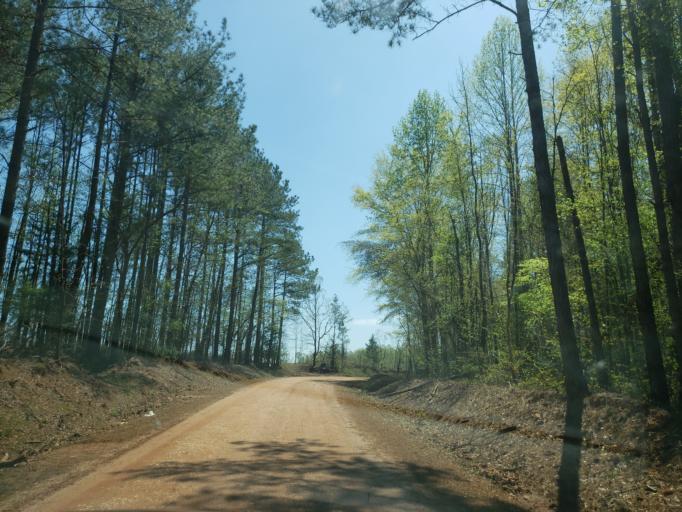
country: US
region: Alabama
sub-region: Tallapoosa County
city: Camp Hill
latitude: 32.6468
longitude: -85.6456
